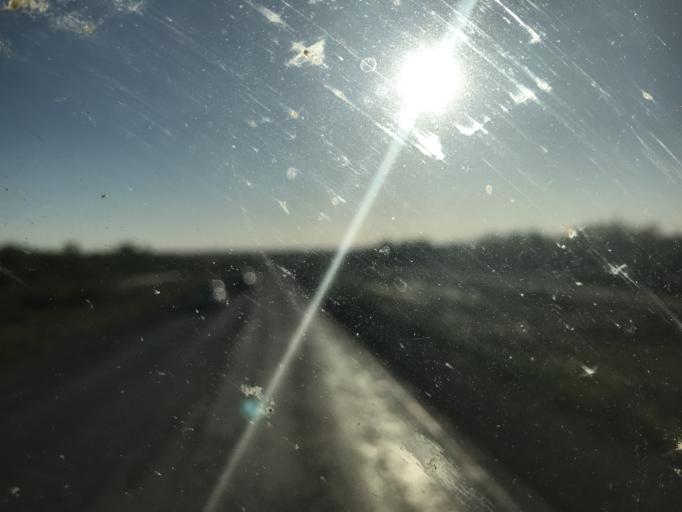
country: KZ
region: Aqtoebe
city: Batamshinskiy
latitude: 50.2844
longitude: 57.8300
